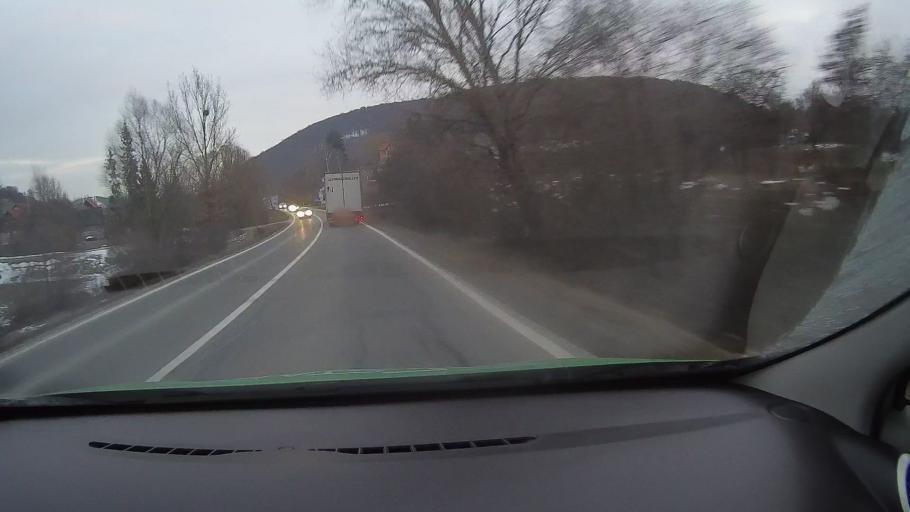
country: RO
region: Harghita
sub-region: Municipiul Odorheiu Secuiesc
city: Odorheiu Secuiesc
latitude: 46.3368
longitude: 25.2701
